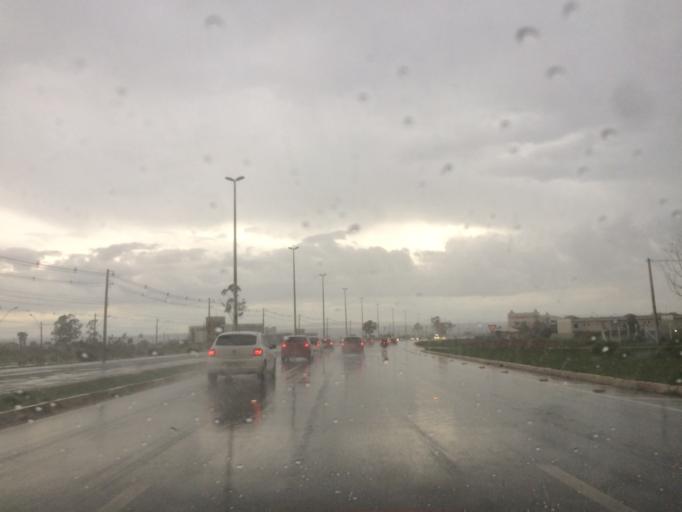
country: BR
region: Federal District
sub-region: Brasilia
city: Brasilia
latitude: -15.8850
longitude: -47.8196
